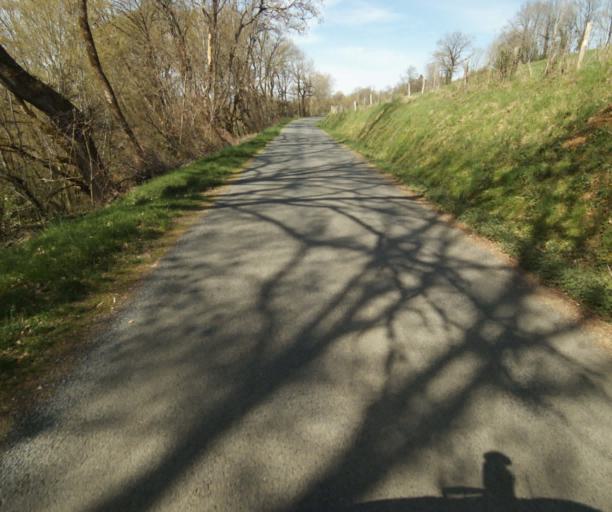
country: FR
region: Limousin
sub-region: Departement de la Correze
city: Naves
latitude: 45.3502
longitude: 1.7779
